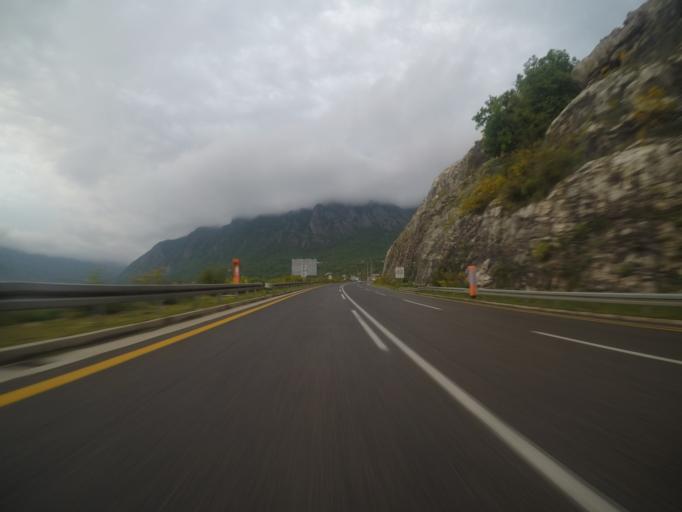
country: ME
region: Bar
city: Sutomore
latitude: 42.2066
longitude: 19.0499
